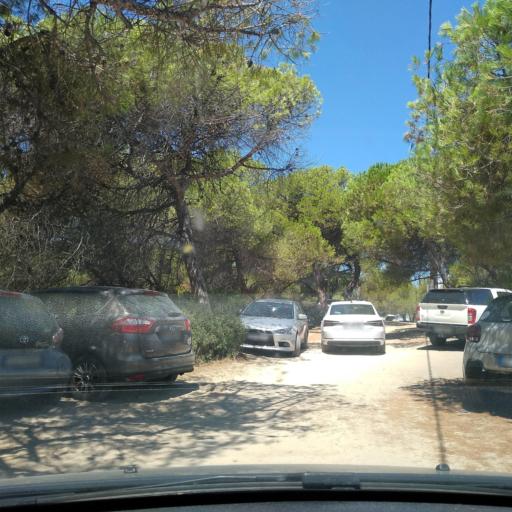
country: GR
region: Central Macedonia
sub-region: Nomos Chalkidikis
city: Neos Marmaras
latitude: 40.1931
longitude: 23.8074
